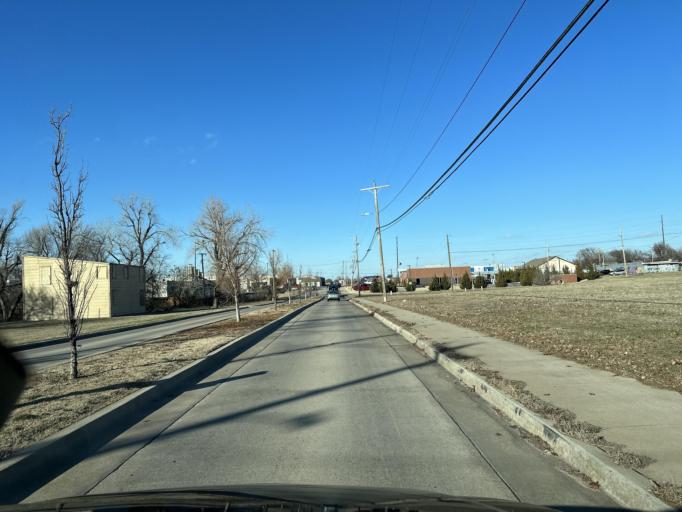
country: US
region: Oklahoma
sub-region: Oklahoma County
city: Midwest City
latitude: 35.4477
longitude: -97.4164
